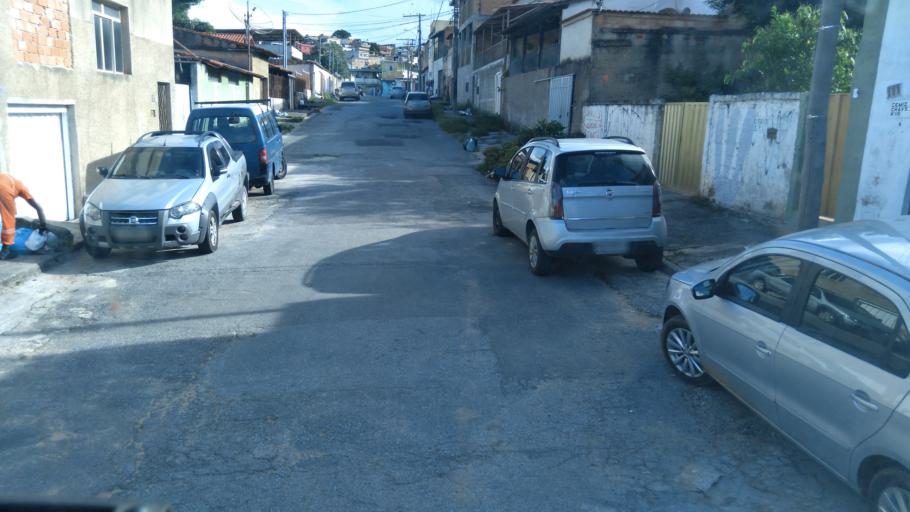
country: BR
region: Minas Gerais
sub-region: Belo Horizonte
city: Belo Horizonte
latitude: -19.8504
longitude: -43.9089
